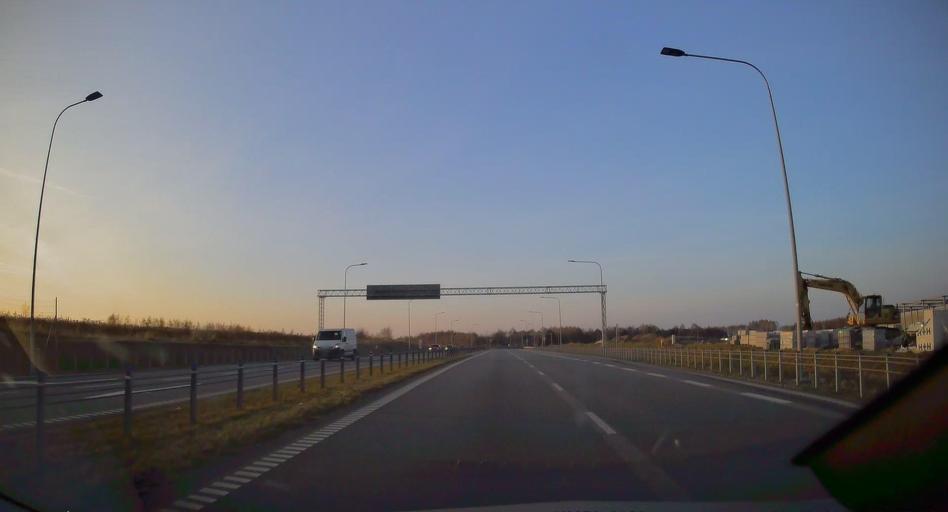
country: PL
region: Silesian Voivodeship
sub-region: Powiat klobucki
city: Kamyk
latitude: 50.8487
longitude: 19.0382
